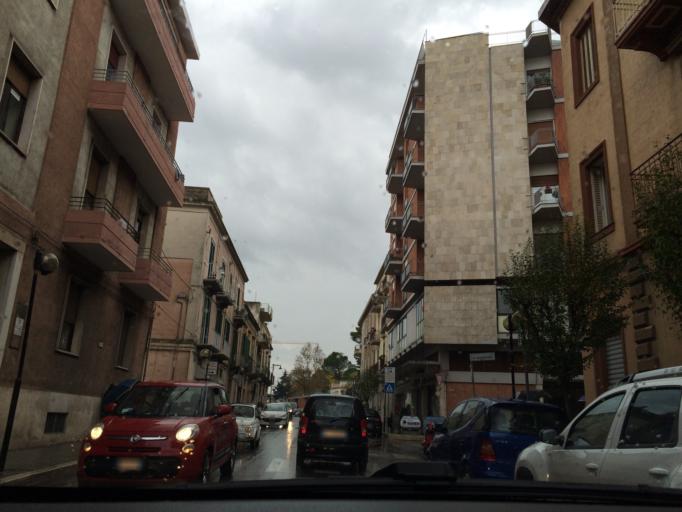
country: IT
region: Basilicate
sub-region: Provincia di Matera
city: Matera
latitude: 40.6660
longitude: 16.6050
